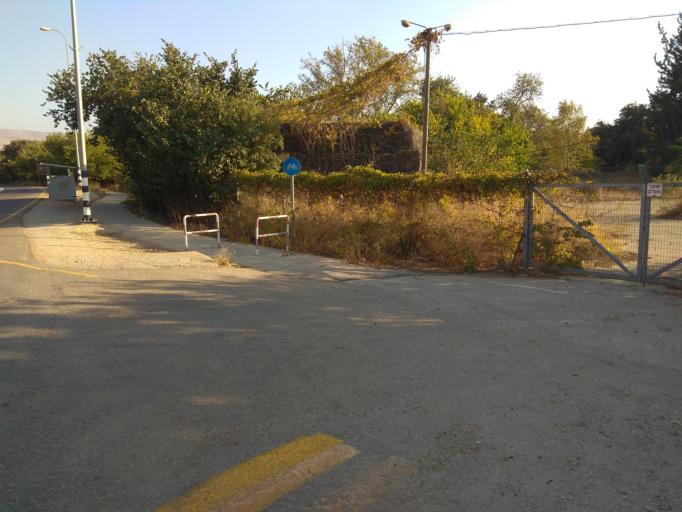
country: IL
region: Northern District
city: Qiryat Shemona
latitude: 33.2237
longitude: 35.6316
